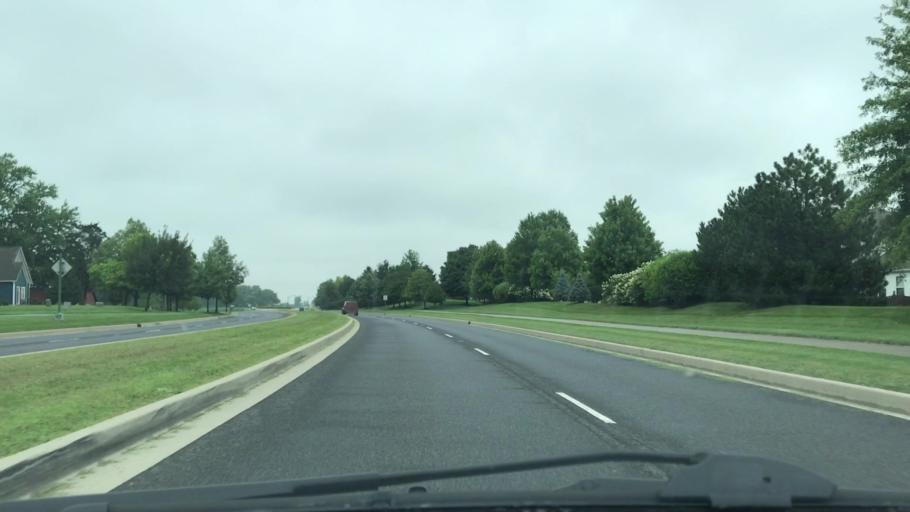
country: US
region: Indiana
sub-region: Hamilton County
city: Westfield
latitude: 40.0606
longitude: -86.0712
